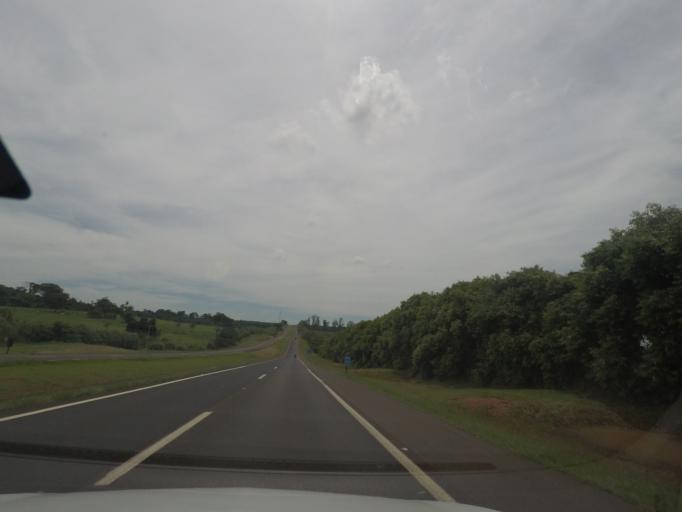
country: BR
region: Sao Paulo
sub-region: Bebedouro
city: Bebedouro
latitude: -21.0039
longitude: -48.4293
